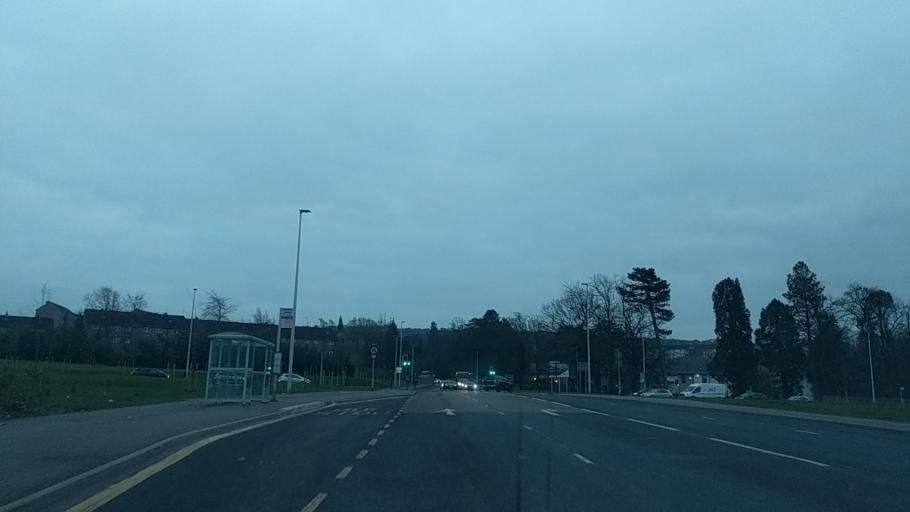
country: GB
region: Scotland
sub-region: South Lanarkshire
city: Rutherglen
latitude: 55.8162
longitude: -4.2147
